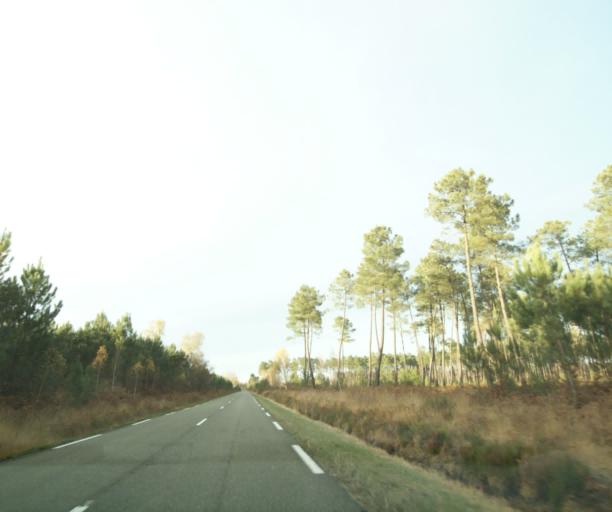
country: FR
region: Aquitaine
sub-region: Departement des Landes
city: Gabarret
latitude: 44.0910
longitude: -0.0966
